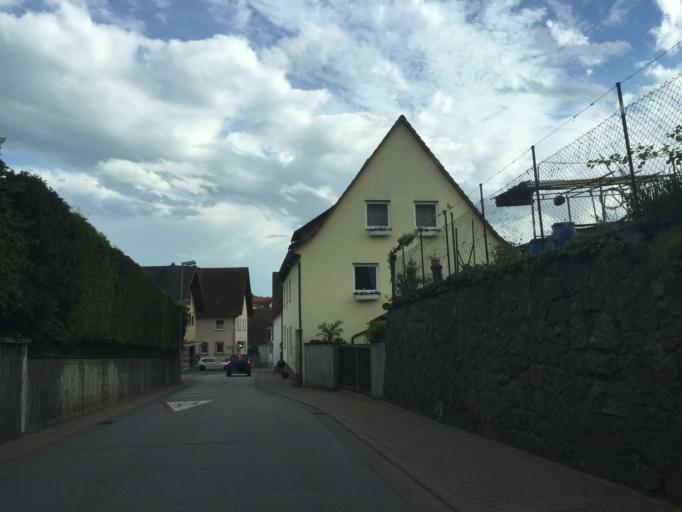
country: DE
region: Baden-Wuerttemberg
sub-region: Karlsruhe Region
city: Weinheim
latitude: 49.5280
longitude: 8.6667
